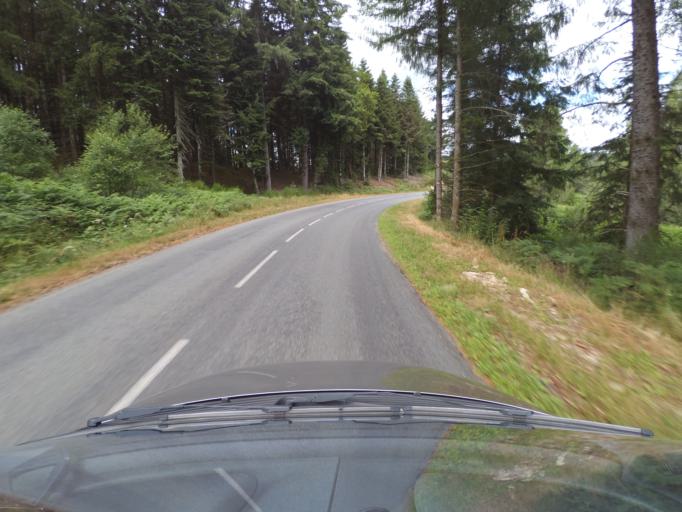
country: FR
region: Limousin
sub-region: Departement de la Haute-Vienne
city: Peyrat-le-Chateau
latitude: 45.8847
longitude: 1.8899
